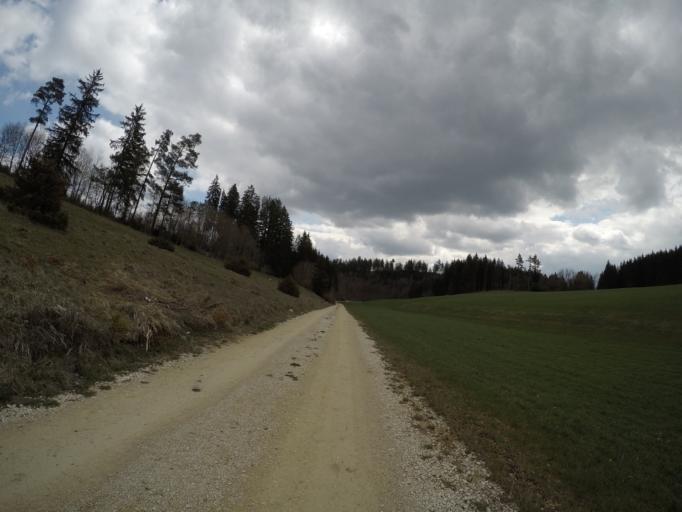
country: DE
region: Baden-Wuerttemberg
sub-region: Tuebingen Region
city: Nellingen
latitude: 48.5041
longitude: 9.7964
